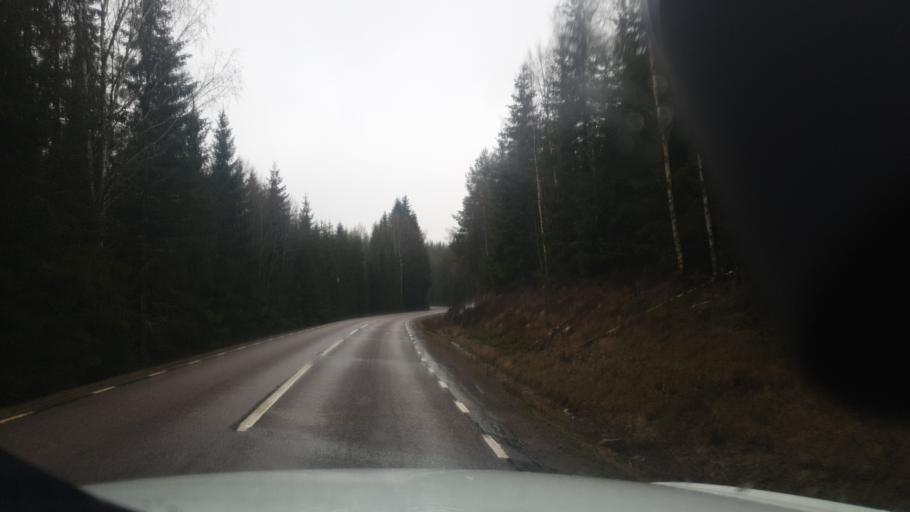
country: SE
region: Vaermland
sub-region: Eda Kommun
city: Amotfors
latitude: 59.6421
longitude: 12.3545
